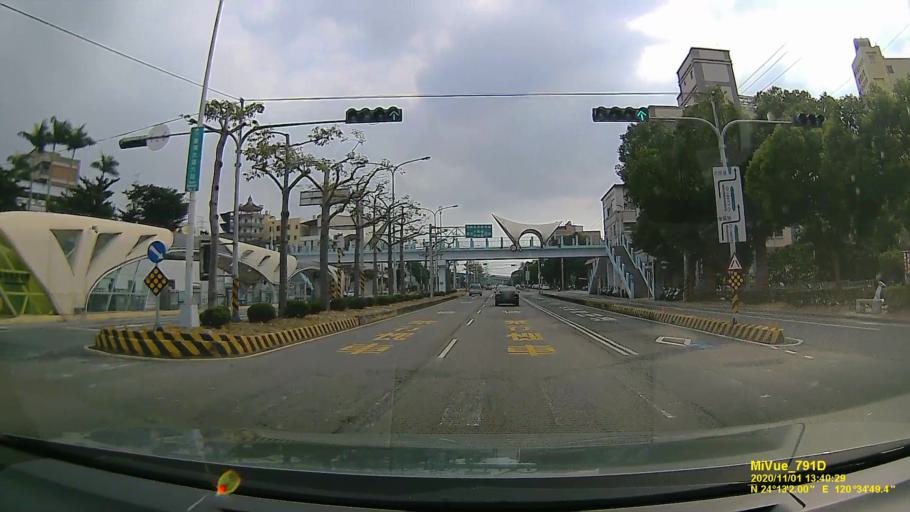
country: TW
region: Taiwan
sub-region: Taichung City
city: Taichung
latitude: 24.2172
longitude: 120.5804
